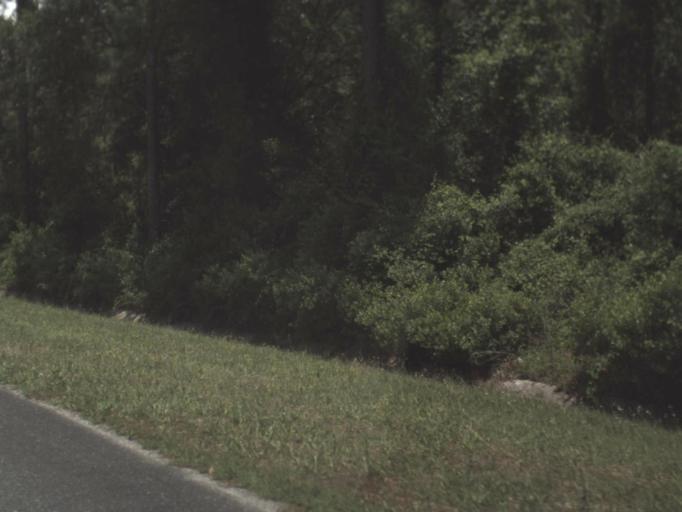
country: US
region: Florida
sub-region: Union County
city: Lake Butler
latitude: 30.0991
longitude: -82.4788
